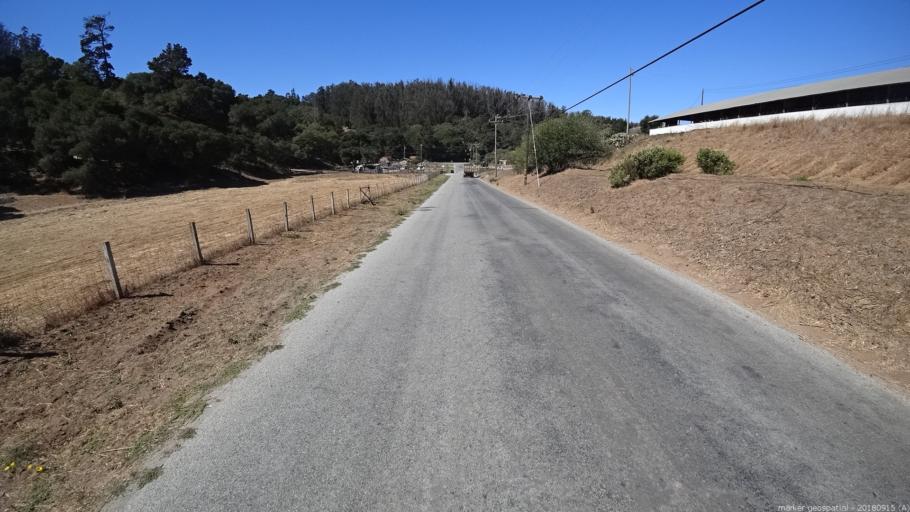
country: US
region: California
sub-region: San Benito County
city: Aromas
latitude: 36.8344
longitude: -121.6648
